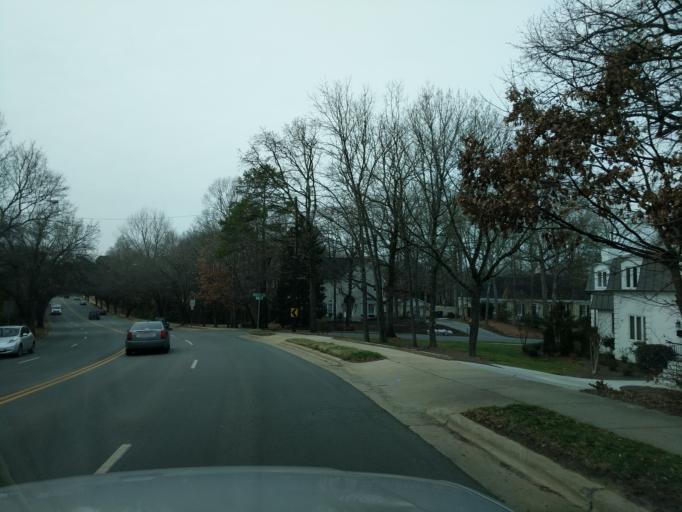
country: US
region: North Carolina
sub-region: Mecklenburg County
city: Charlotte
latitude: 35.1820
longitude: -80.8120
